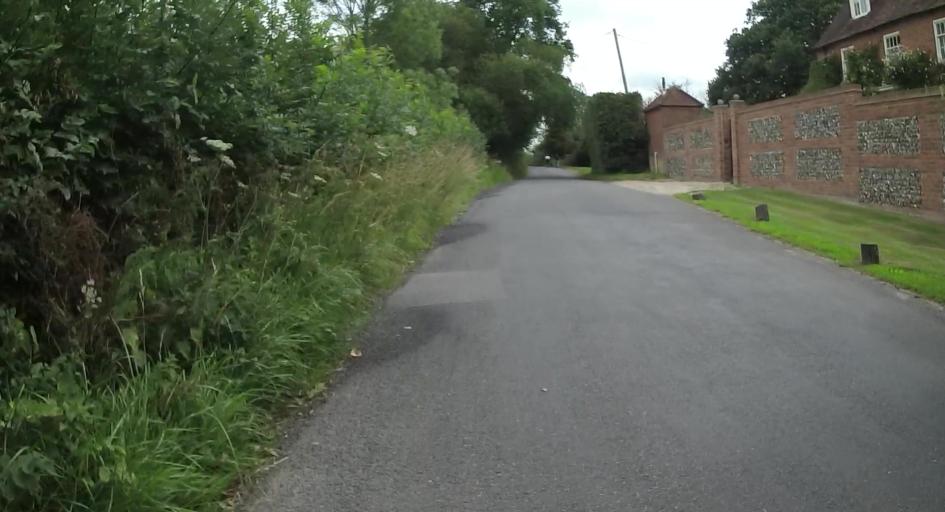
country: GB
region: England
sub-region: West Berkshire
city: Stratfield Mortimer
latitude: 51.3449
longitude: -1.0421
